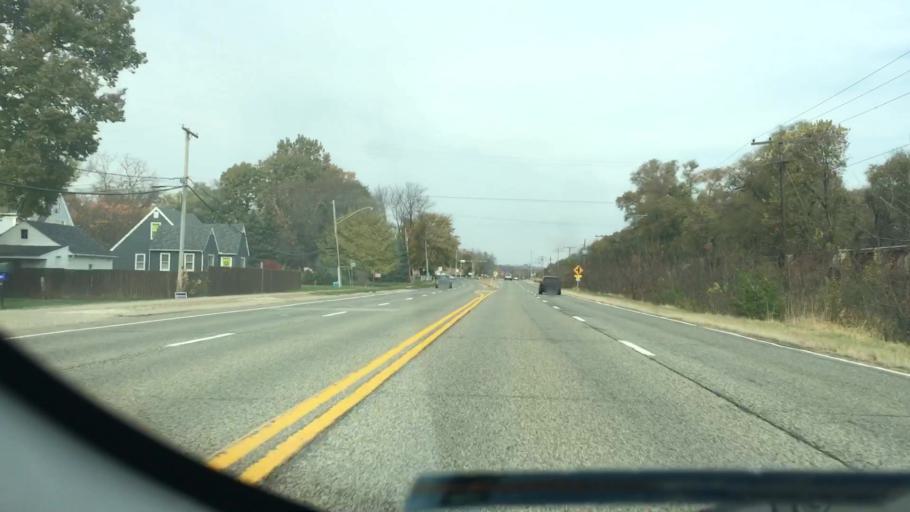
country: US
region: Illinois
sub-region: Peoria County
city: Peoria Heights
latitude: 40.7558
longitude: -89.5632
